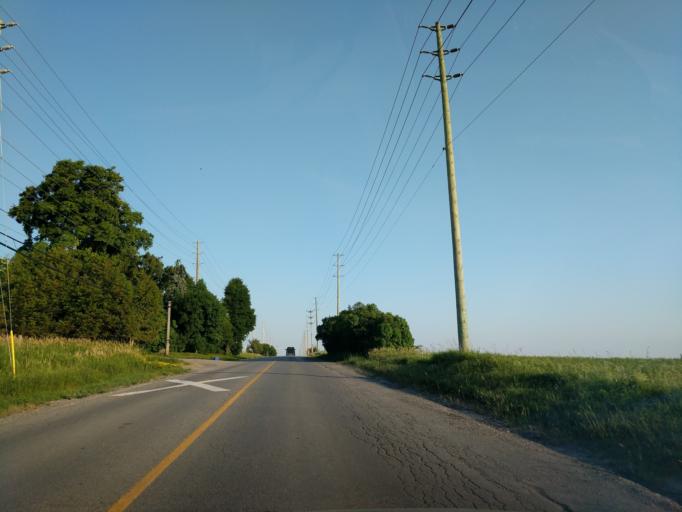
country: CA
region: Ontario
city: Oshawa
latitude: 43.8805
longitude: -78.8883
